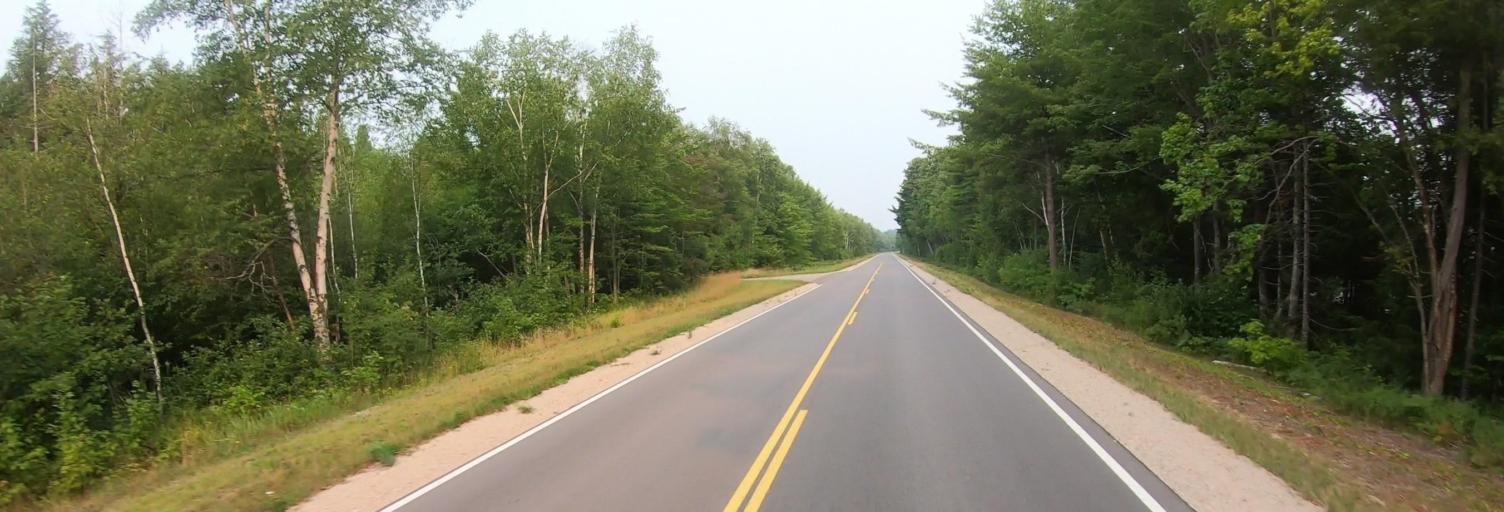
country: US
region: Michigan
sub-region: Luce County
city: Newberry
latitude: 46.4799
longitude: -85.0171
